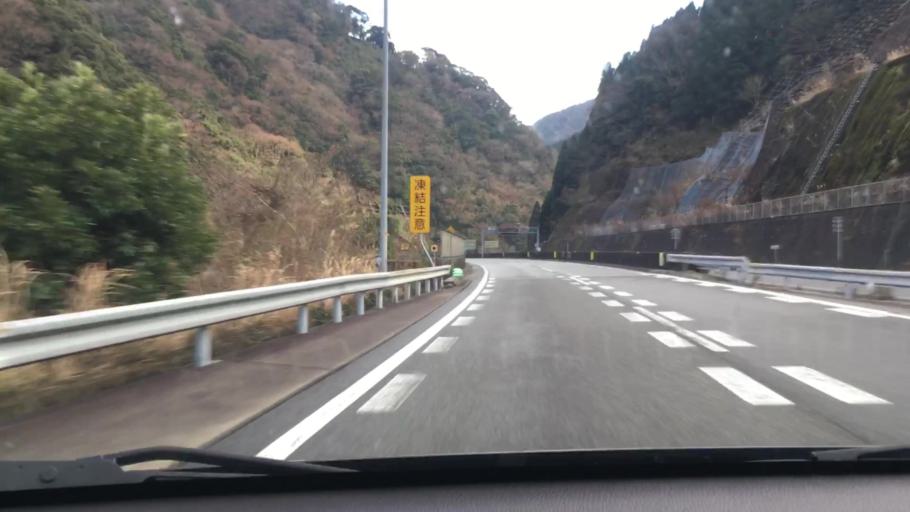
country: JP
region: Kumamoto
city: Hitoyoshi
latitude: 32.3387
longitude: 130.7316
